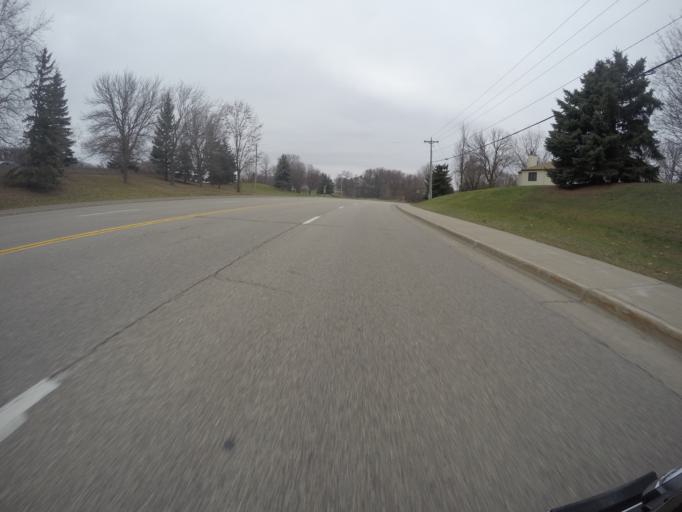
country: US
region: Minnesota
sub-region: Hennepin County
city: Hopkins
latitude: 44.8894
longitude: -93.4468
